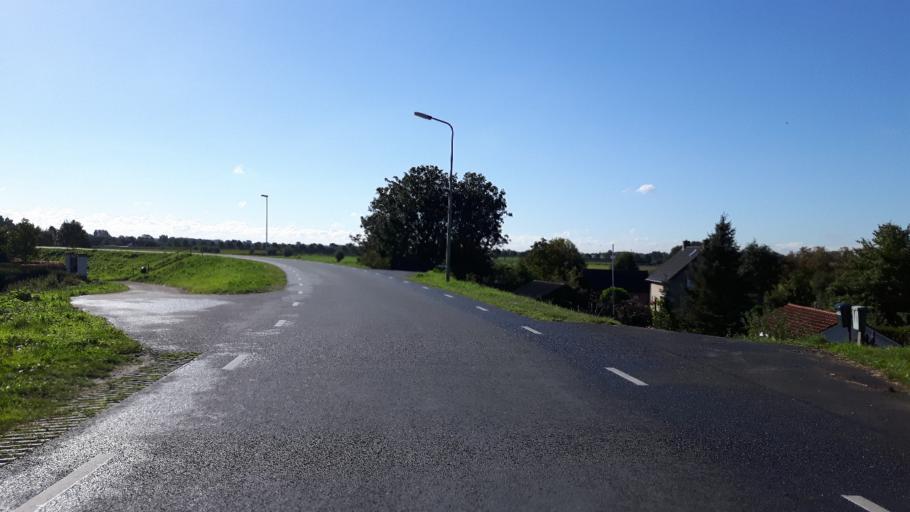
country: NL
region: Utrecht
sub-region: Gemeente Vianen
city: Vianen
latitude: 51.9842
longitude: 5.1338
